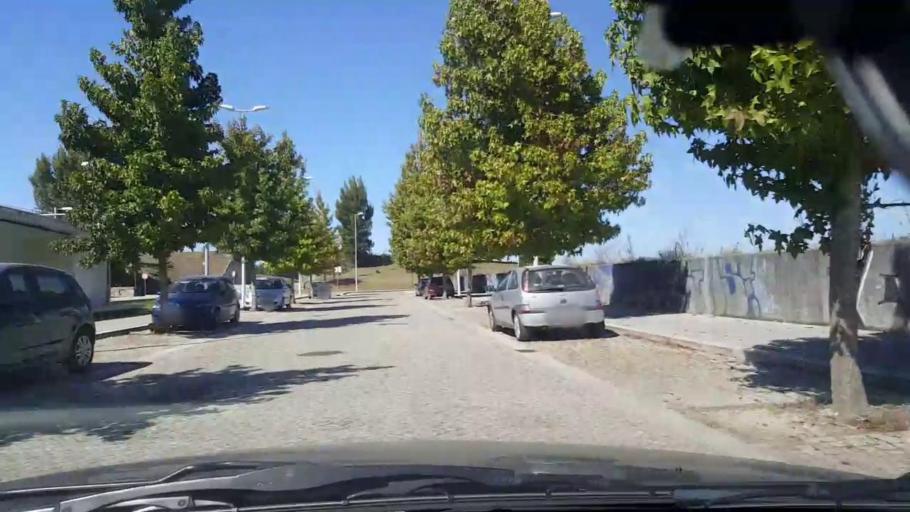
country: PT
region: Porto
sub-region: Matosinhos
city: Lavra
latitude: 41.2850
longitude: -8.6932
